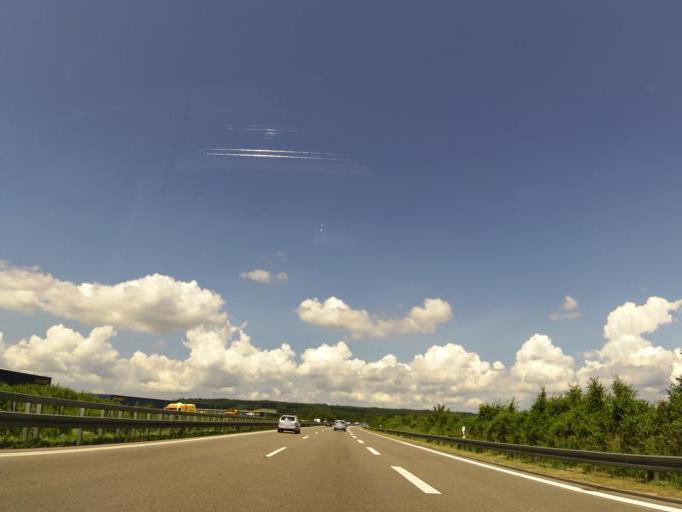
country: DE
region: Baden-Wuerttemberg
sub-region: Tuebingen Region
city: Langenau
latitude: 48.4891
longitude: 10.0920
